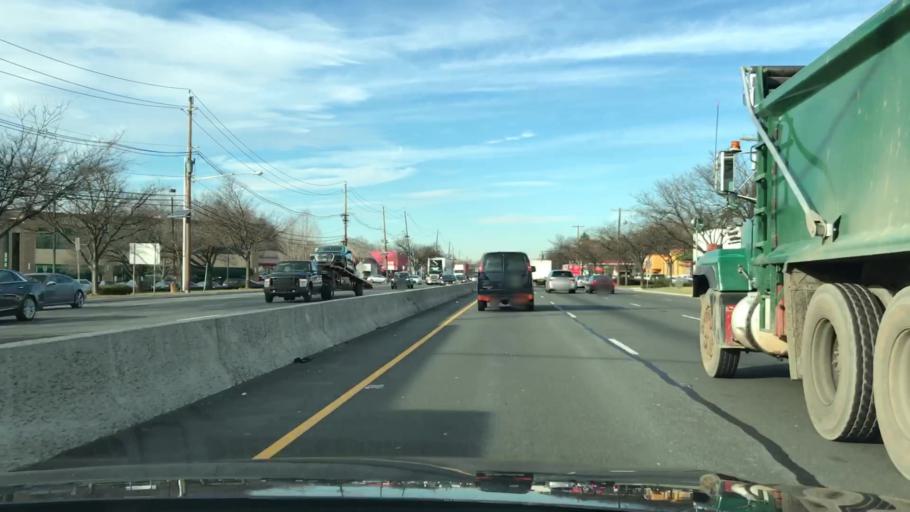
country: US
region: New Jersey
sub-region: Bergen County
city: Paramus
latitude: 40.9721
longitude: -74.0803
